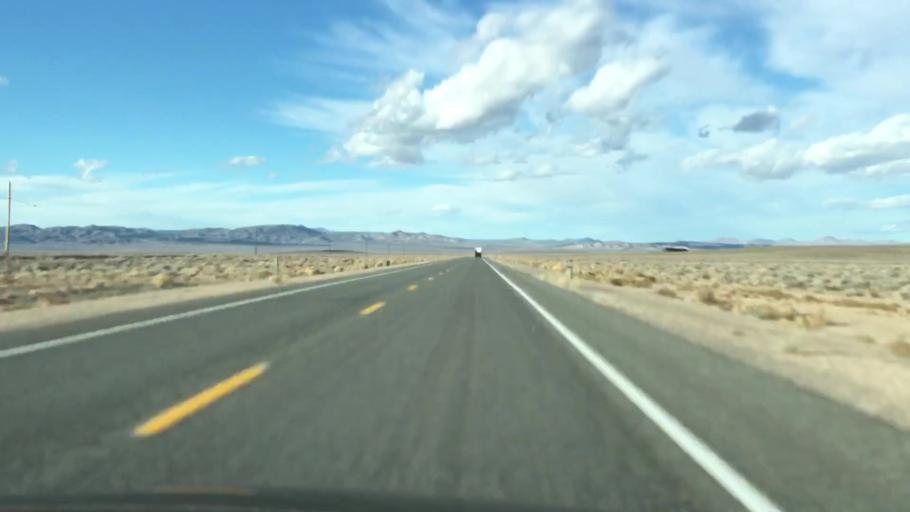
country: US
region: Nevada
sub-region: Esmeralda County
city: Goldfield
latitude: 37.4112
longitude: -117.1529
